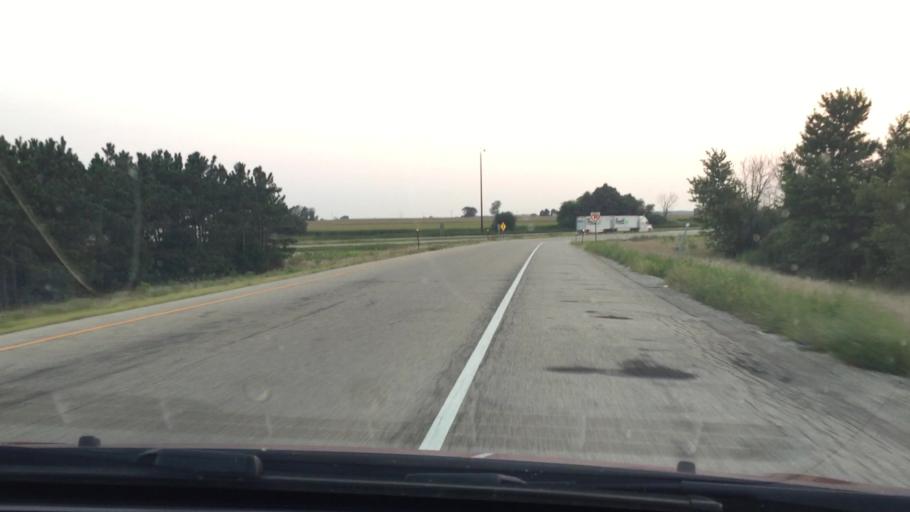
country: US
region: Illinois
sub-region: Bureau County
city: Ladd
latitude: 41.3693
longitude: -89.2199
